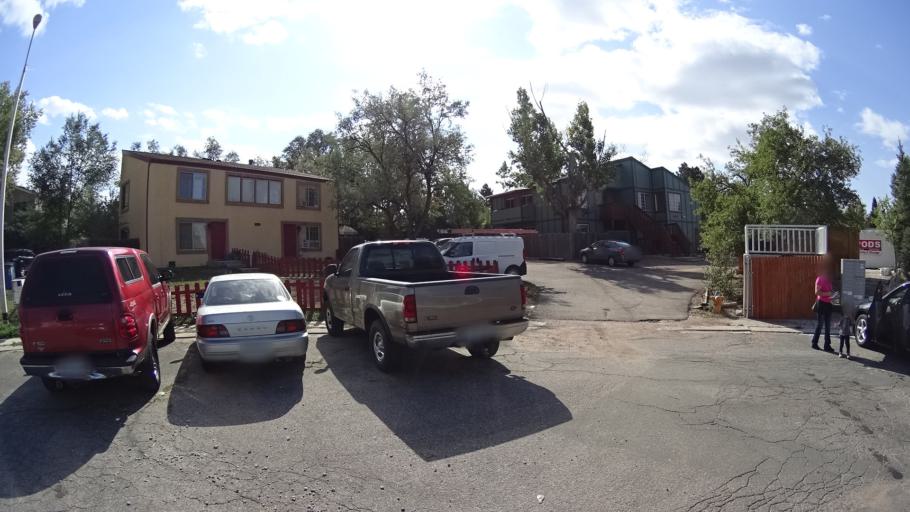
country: US
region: Colorado
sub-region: El Paso County
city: Cimarron Hills
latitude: 38.8853
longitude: -104.7409
